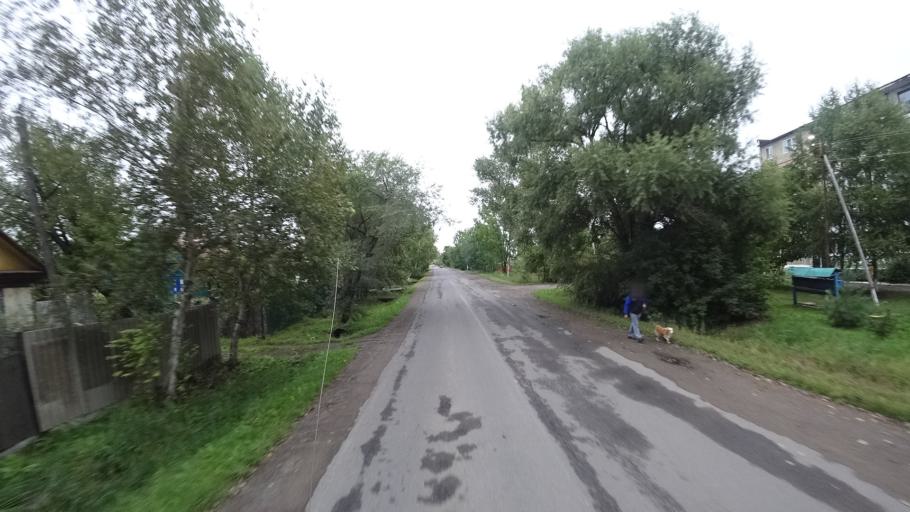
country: RU
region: Primorskiy
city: Chernigovka
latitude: 44.3364
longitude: 132.5312
